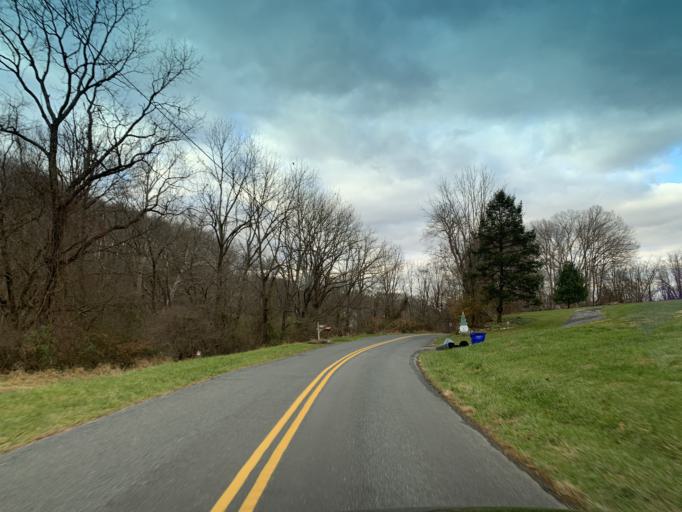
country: US
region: Maryland
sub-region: Harford County
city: Jarrettsville
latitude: 39.6502
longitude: -76.4365
